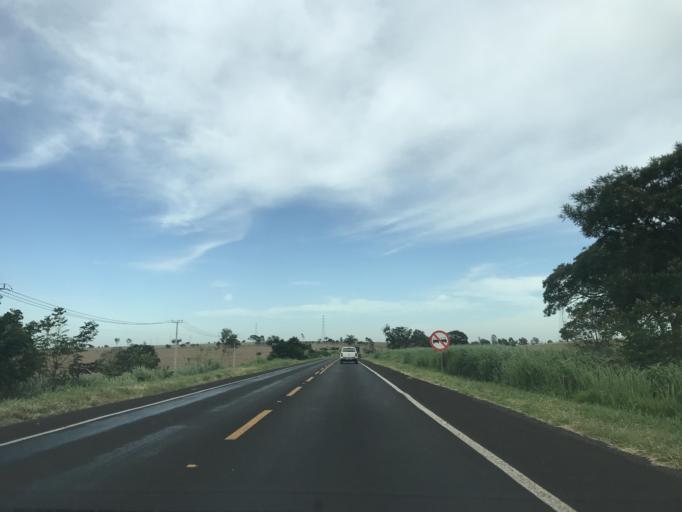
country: BR
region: Parana
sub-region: Paranavai
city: Paranavai
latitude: -23.0150
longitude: -52.5249
